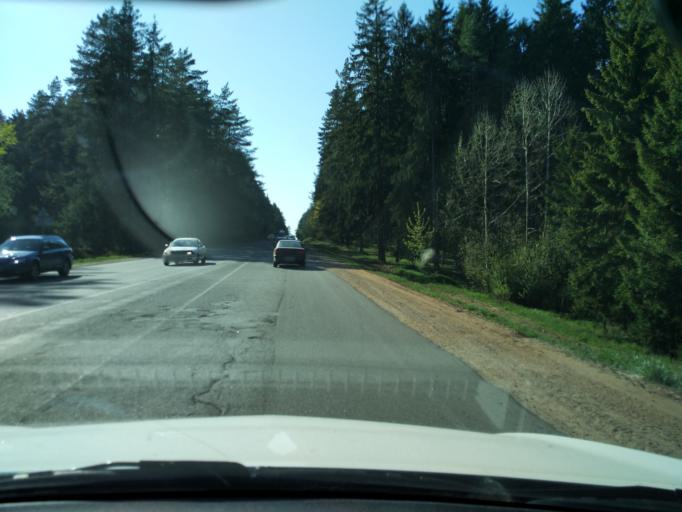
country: BY
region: Minsk
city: Borovlyany
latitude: 53.9616
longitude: 27.6887
